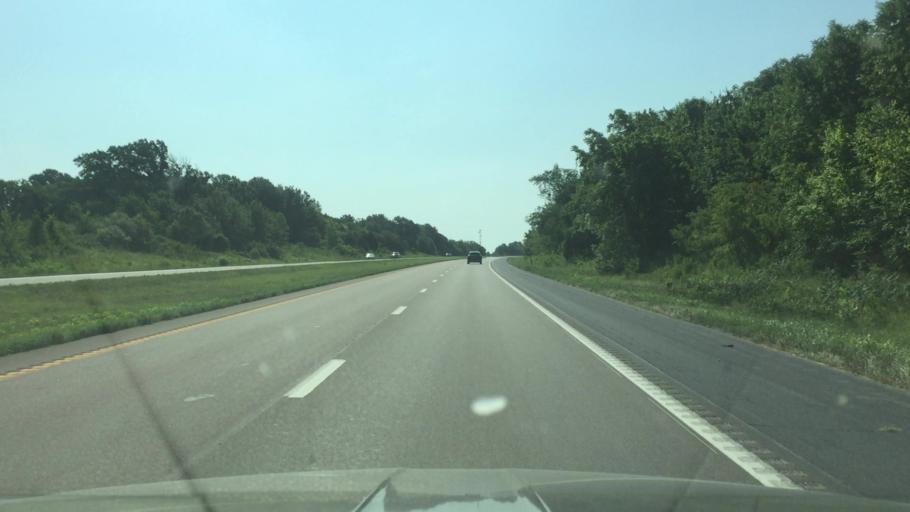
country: US
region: Missouri
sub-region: Pettis County
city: Sedalia
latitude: 38.7413
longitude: -93.3246
